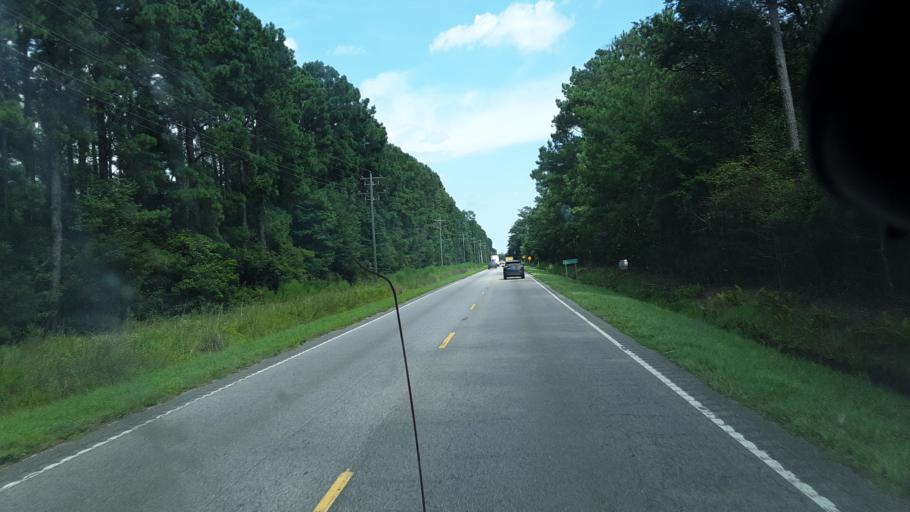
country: US
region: South Carolina
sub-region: Horry County
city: Red Hill
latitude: 33.8222
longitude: -78.9191
